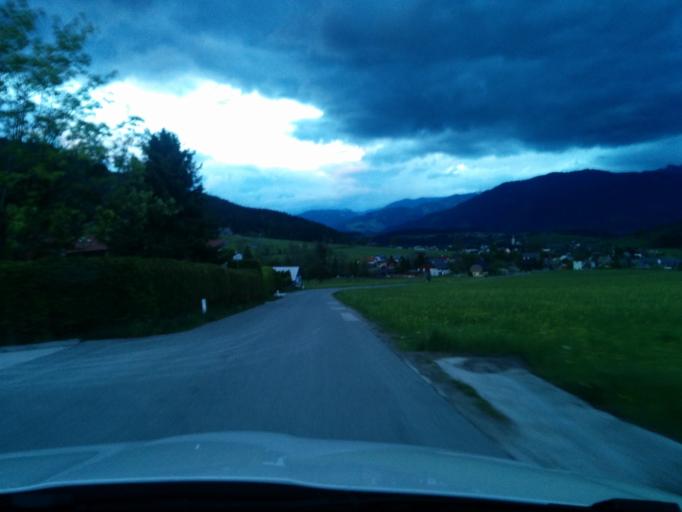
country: AT
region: Styria
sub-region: Politischer Bezirk Liezen
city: Pruggern
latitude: 47.4491
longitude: 13.8668
